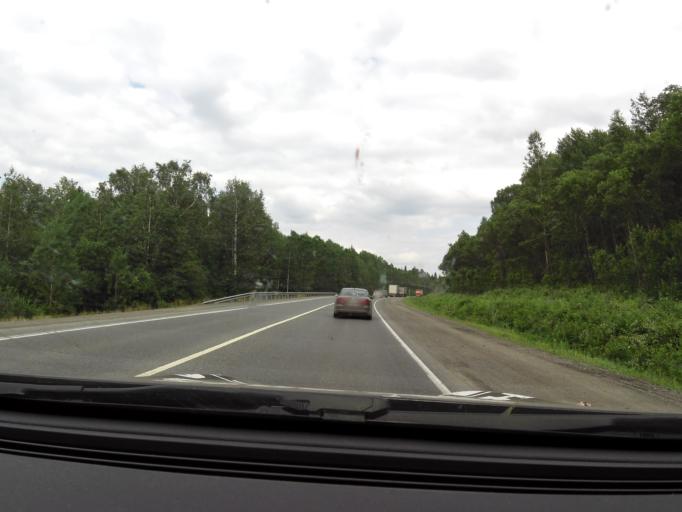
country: RU
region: Sverdlovsk
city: Bilimbay
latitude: 56.8593
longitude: 59.7208
